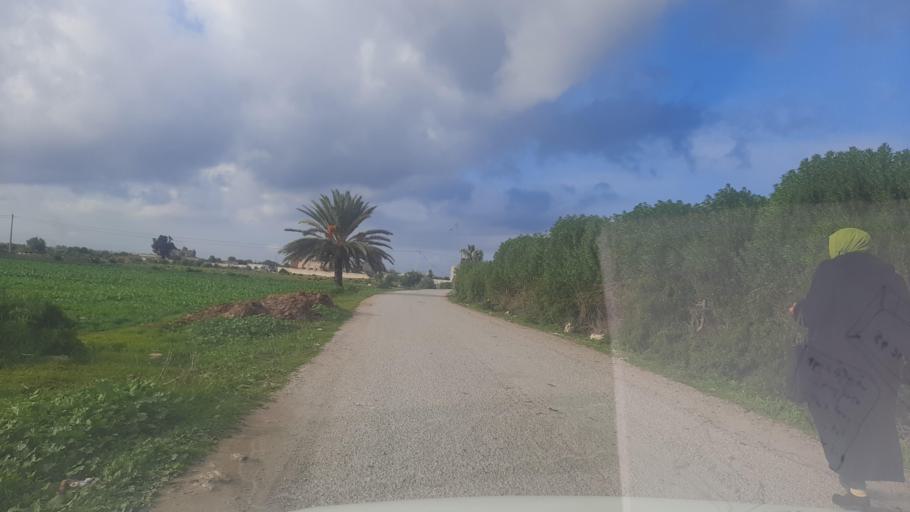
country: TN
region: Nabul
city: Manzil Bu Zalafah
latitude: 36.7138
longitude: 10.4984
